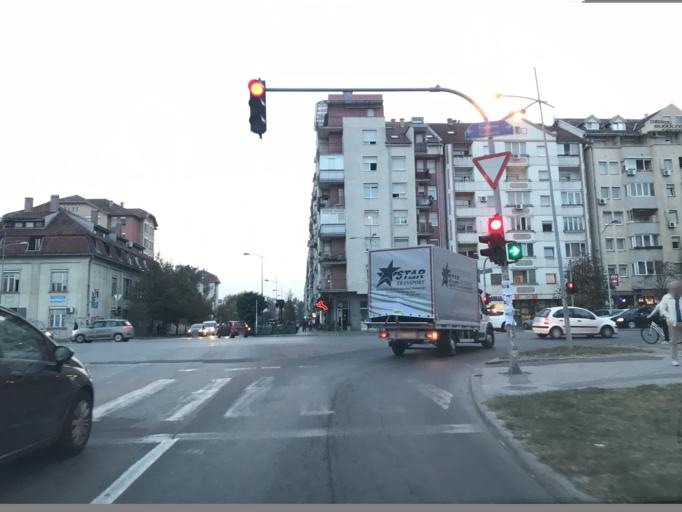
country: RS
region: Autonomna Pokrajina Vojvodina
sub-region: Juznobacki Okrug
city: Novi Sad
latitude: 45.2630
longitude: 19.8190
